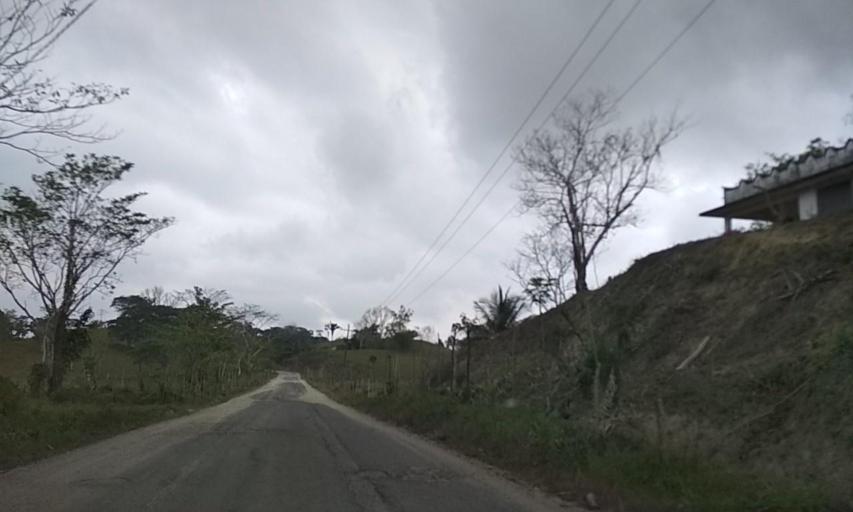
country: MX
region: Tabasco
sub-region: Huimanguillo
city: Francisco Rueda
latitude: 17.6364
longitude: -94.0915
